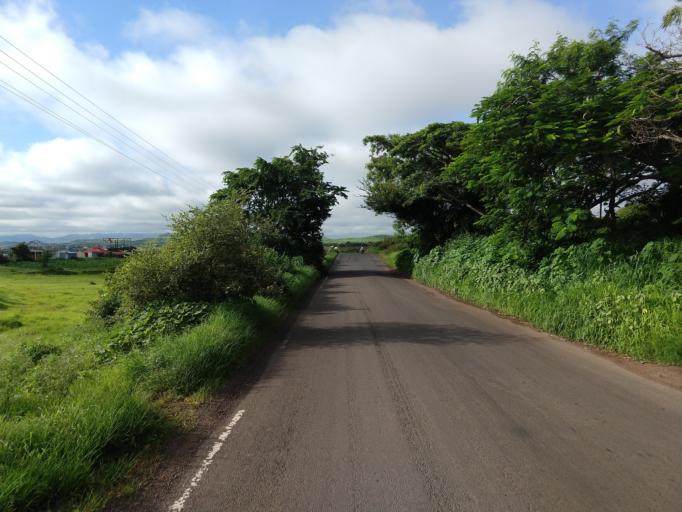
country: IN
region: Maharashtra
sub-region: Pune Division
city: Khed
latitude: 18.4006
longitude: 73.9124
